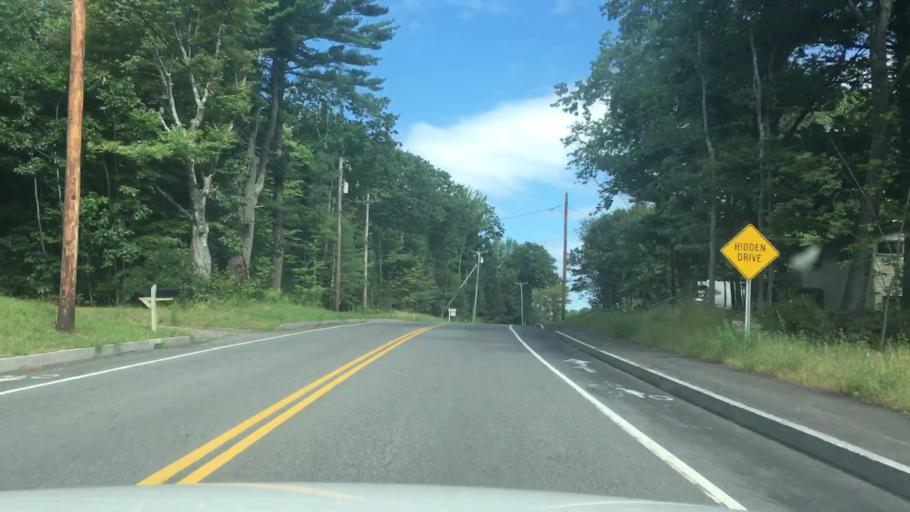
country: US
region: Maine
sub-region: Androscoggin County
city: Auburn
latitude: 44.1104
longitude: -70.2500
